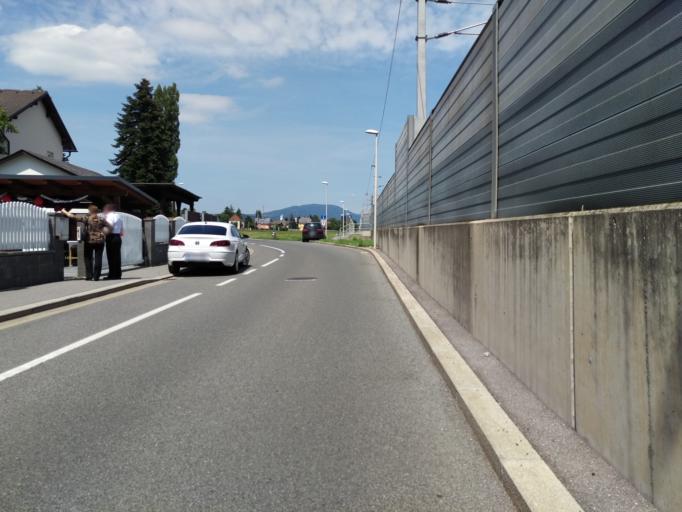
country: AT
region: Styria
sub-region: Graz Stadt
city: Wetzelsdorf
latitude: 47.0504
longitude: 15.4193
